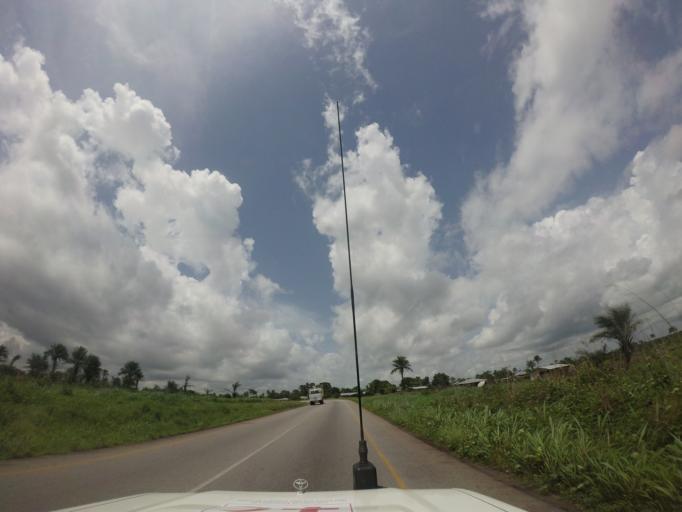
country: SL
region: Northern Province
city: Lunsar
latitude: 8.4853
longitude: -12.6089
